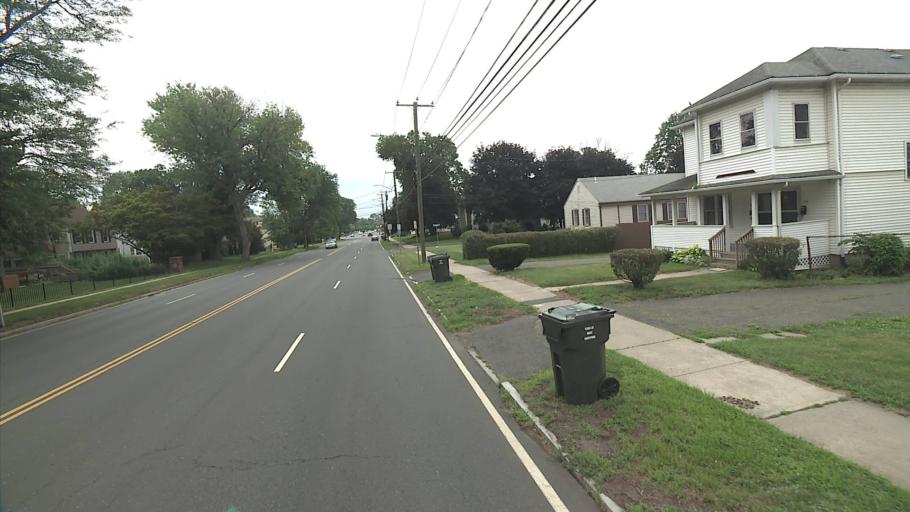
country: US
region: Connecticut
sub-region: Hartford County
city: West Hartford
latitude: 41.7322
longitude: -72.7379
